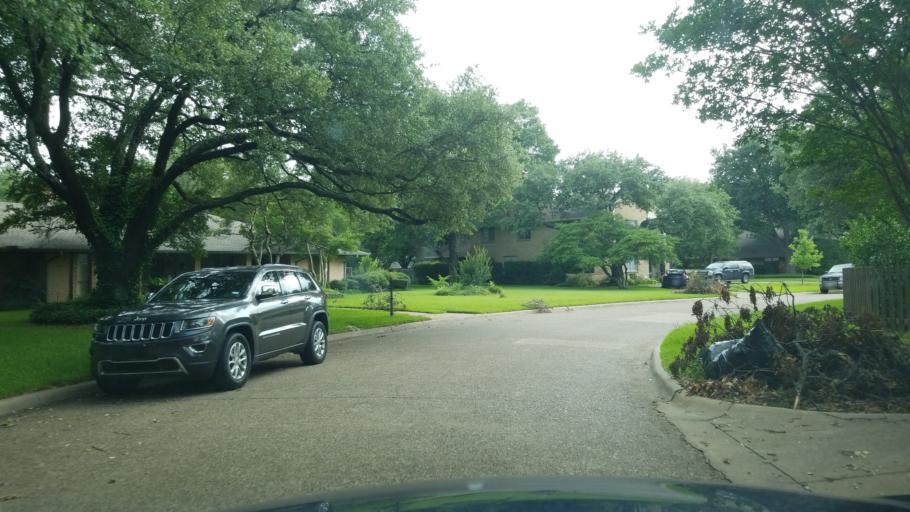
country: US
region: Texas
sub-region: Dallas County
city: University Park
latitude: 32.8993
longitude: -96.8353
